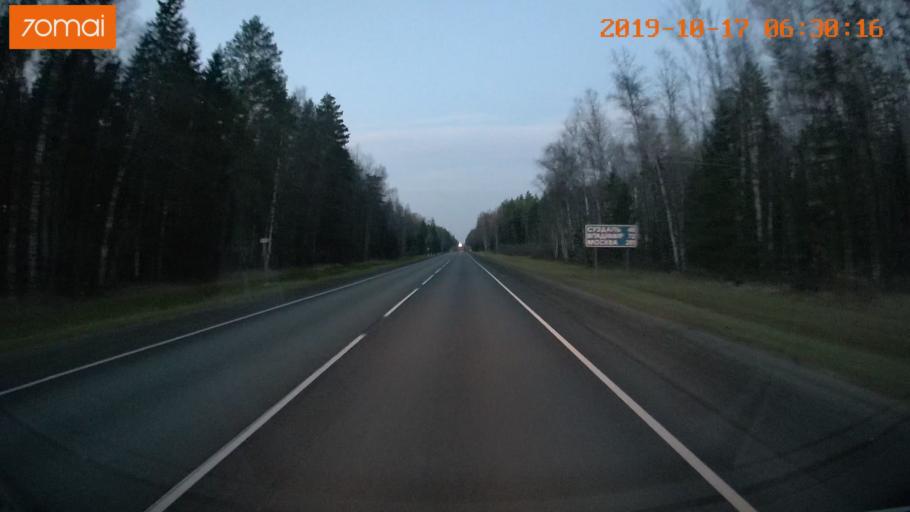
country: RU
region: Ivanovo
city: Lezhnevo
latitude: 56.7378
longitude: 40.7242
